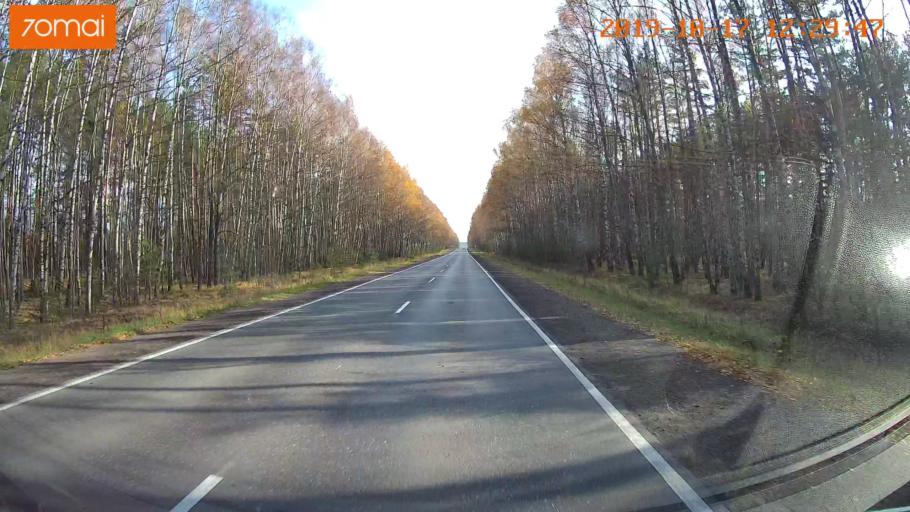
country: RU
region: Rjazan
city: Syntul
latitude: 54.9792
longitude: 41.3003
